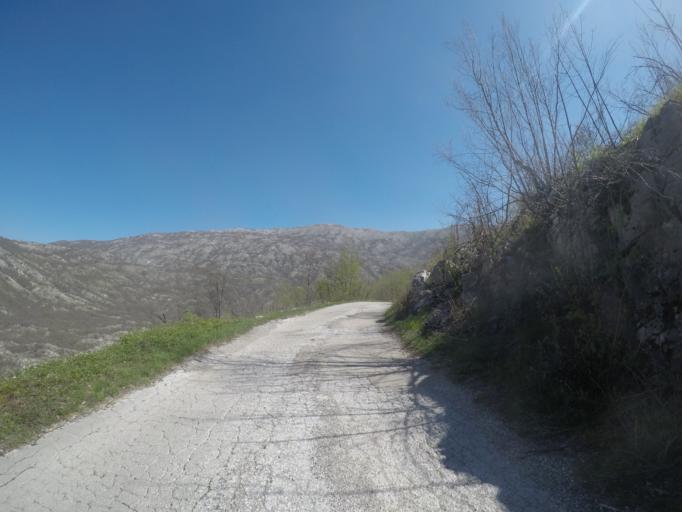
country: ME
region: Danilovgrad
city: Danilovgrad
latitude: 42.5381
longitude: 18.9931
